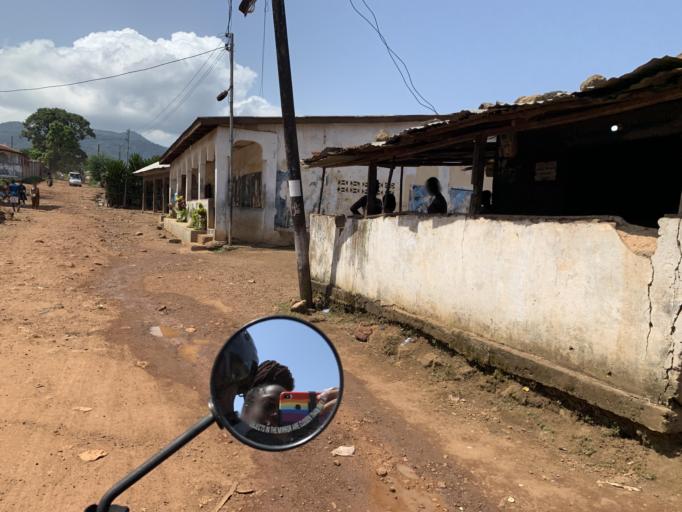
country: SL
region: Western Area
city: Hastings
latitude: 8.3839
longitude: -13.1385
